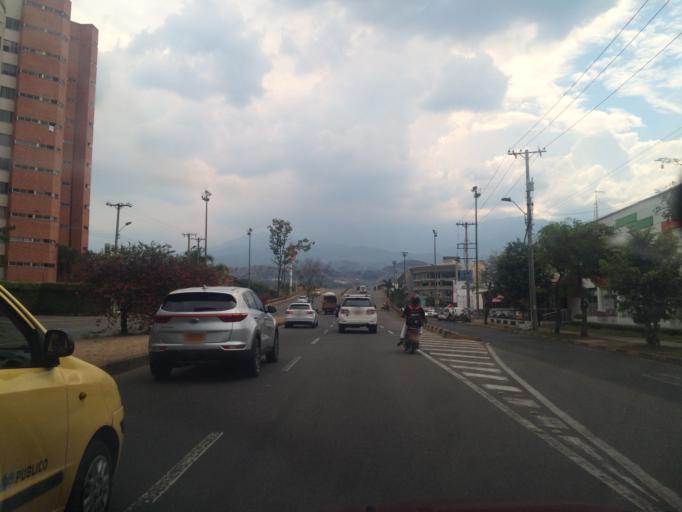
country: CO
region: Valle del Cauca
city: Cali
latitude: 3.3872
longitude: -76.5365
